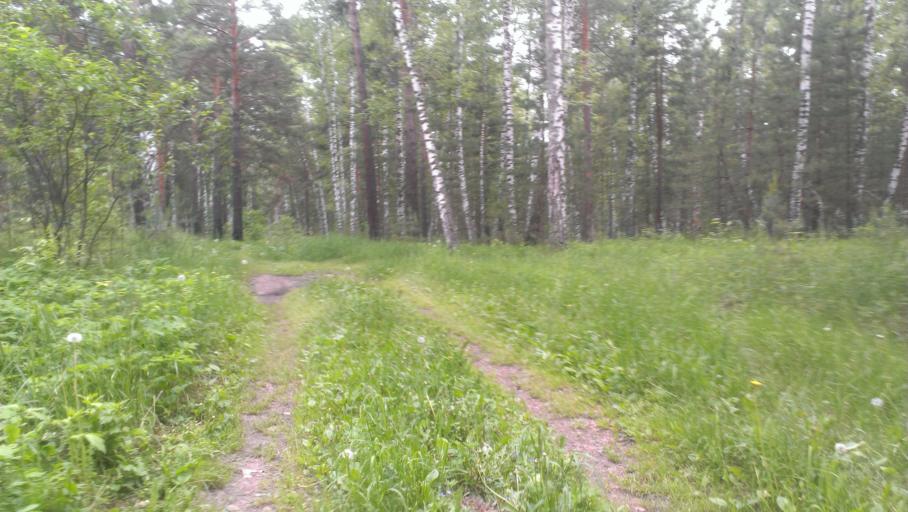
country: RU
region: Altai Krai
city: Sannikovo
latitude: 53.3427
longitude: 84.0455
